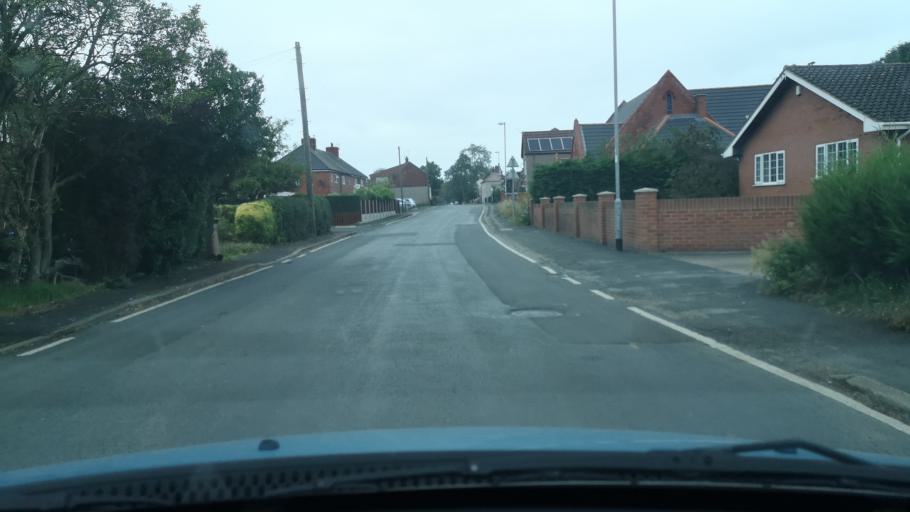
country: GB
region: England
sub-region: East Riding of Yorkshire
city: Laxton
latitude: 53.6979
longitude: -0.7926
